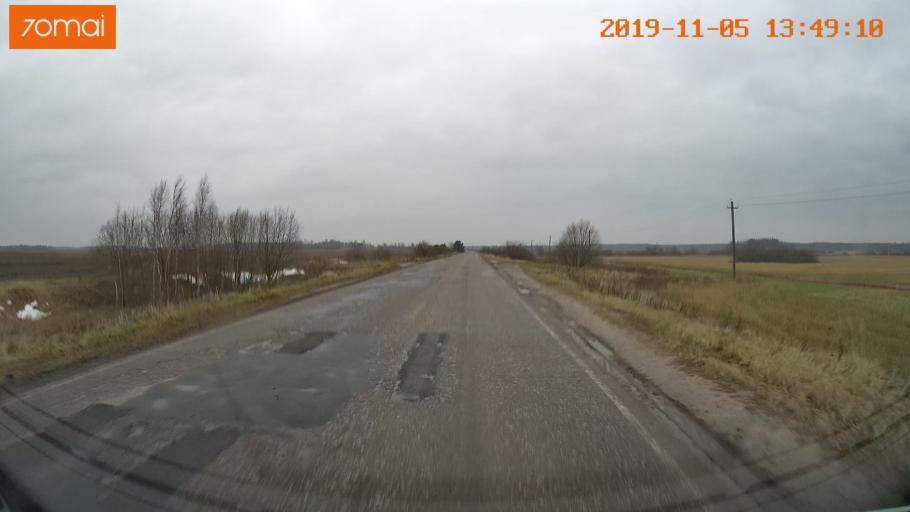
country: RU
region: Ivanovo
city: Kaminskiy
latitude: 57.0080
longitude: 41.4085
